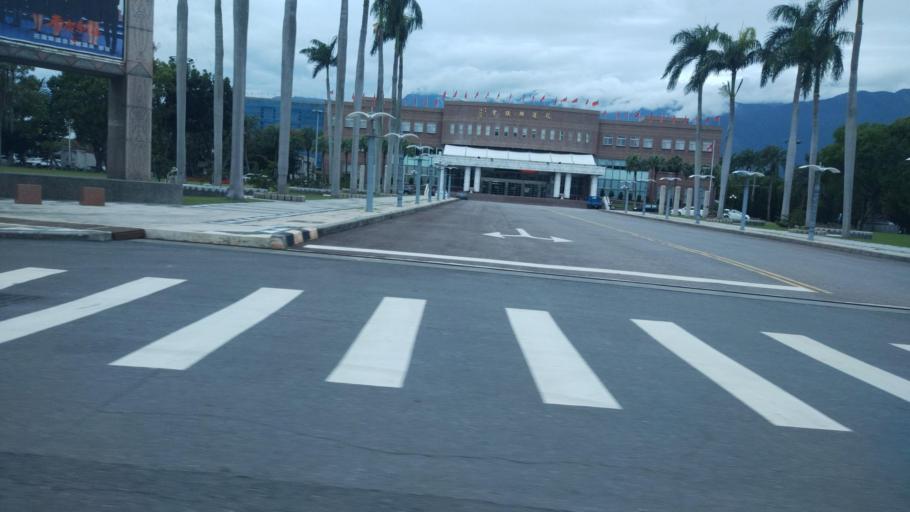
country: TW
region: Taiwan
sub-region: Hualien
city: Hualian
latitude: 23.9939
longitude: 121.6221
